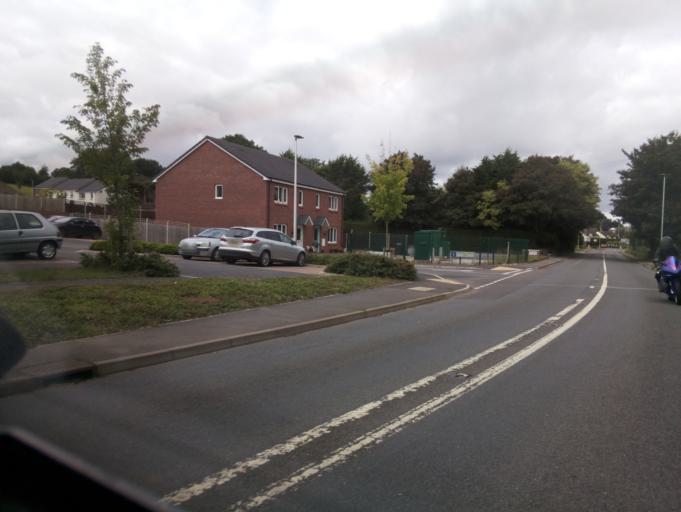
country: GB
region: England
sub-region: Devon
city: Cullompton
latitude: 50.8476
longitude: -3.3933
